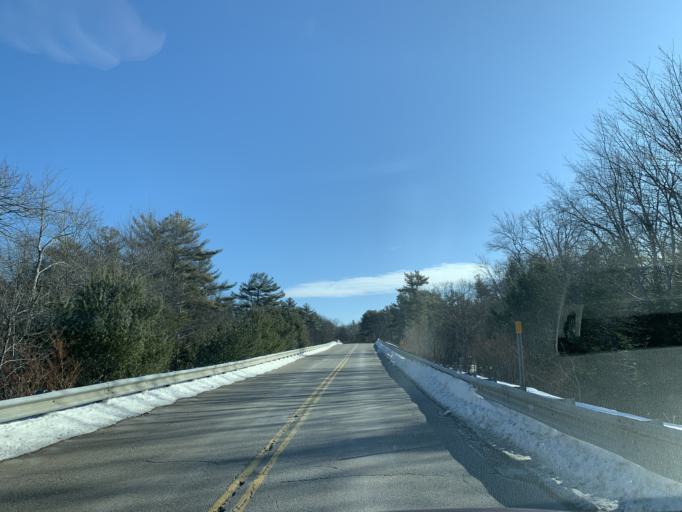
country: US
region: Maine
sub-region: York County
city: Ogunquit
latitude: 43.2493
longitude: -70.6270
